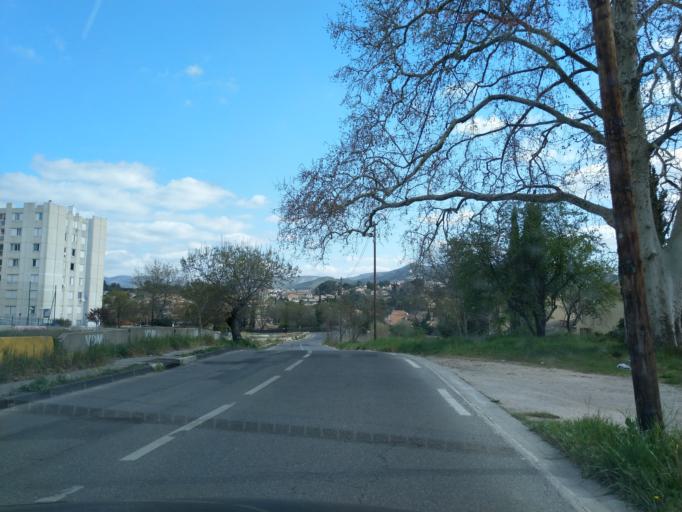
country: FR
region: Provence-Alpes-Cote d'Azur
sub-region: Departement des Bouches-du-Rhone
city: Plan-de-Cuques
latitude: 43.3288
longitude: 5.4557
